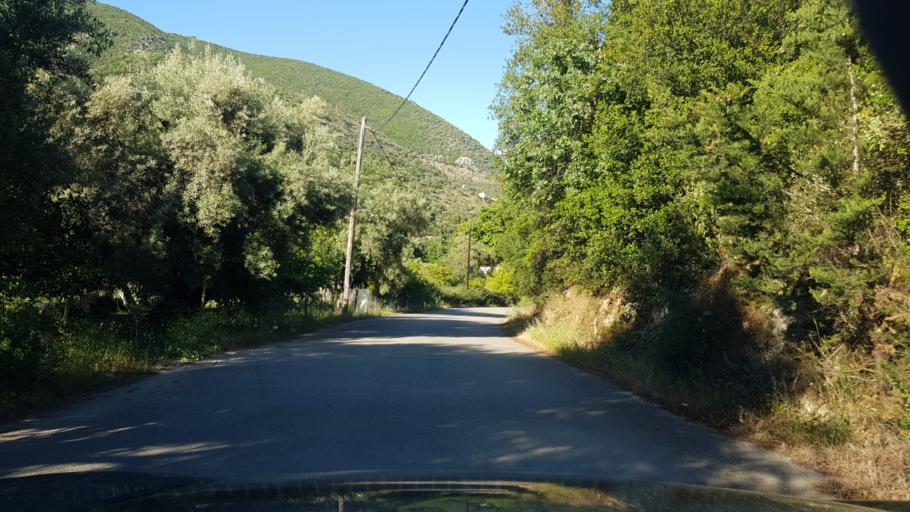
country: GR
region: Ionian Islands
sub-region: Lefkada
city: Nidri
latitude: 38.7152
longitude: 20.6973
